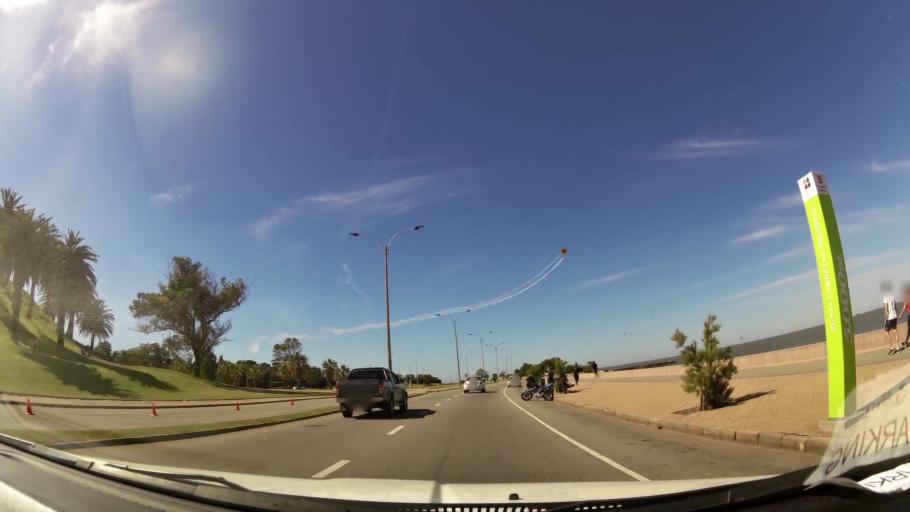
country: UY
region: Montevideo
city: Montevideo
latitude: -34.9210
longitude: -56.1710
